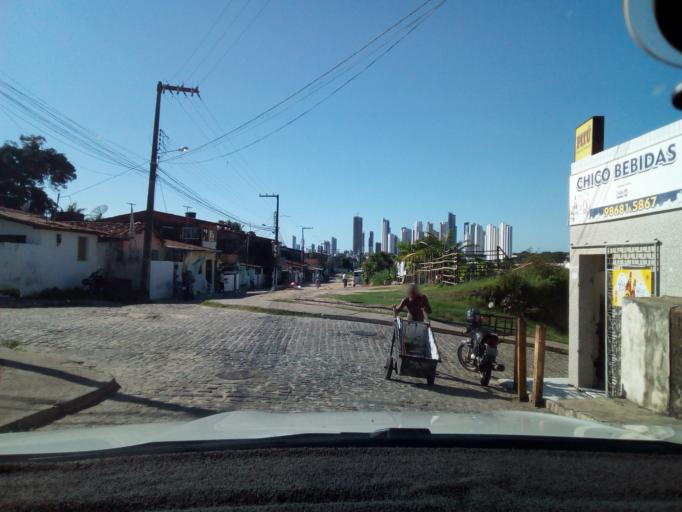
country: BR
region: Paraiba
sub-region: Joao Pessoa
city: Joao Pessoa
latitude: -7.1497
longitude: -34.8301
